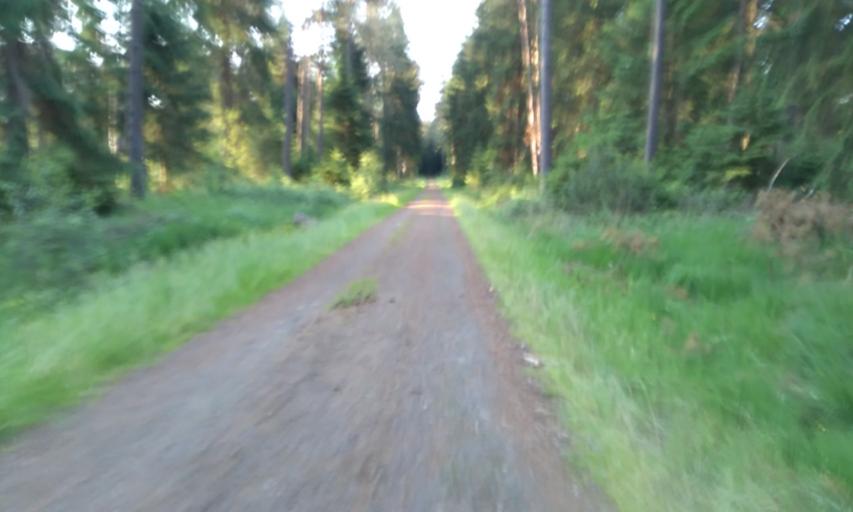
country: DE
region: Lower Saxony
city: Dollern
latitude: 53.5290
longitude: 9.5149
